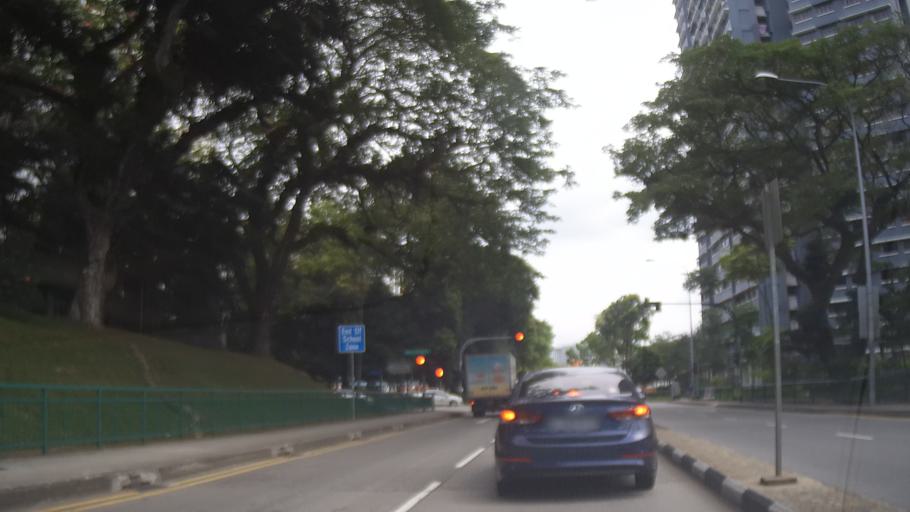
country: MY
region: Johor
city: Johor Bahru
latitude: 1.4393
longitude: 103.7776
